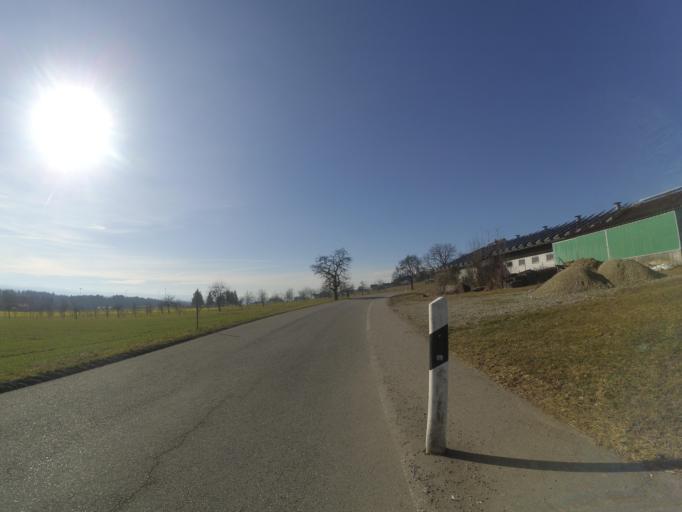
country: DE
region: Baden-Wuerttemberg
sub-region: Tuebingen Region
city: Wolpertswende
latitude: 47.8985
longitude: 9.6177
